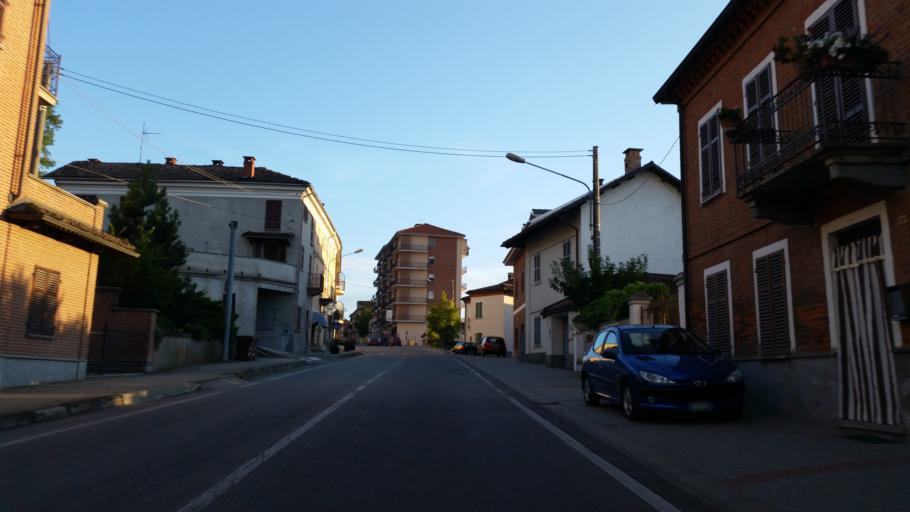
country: IT
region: Piedmont
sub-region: Provincia di Asti
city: Piano-Molini d'Isola
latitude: 44.8311
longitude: 8.1789
